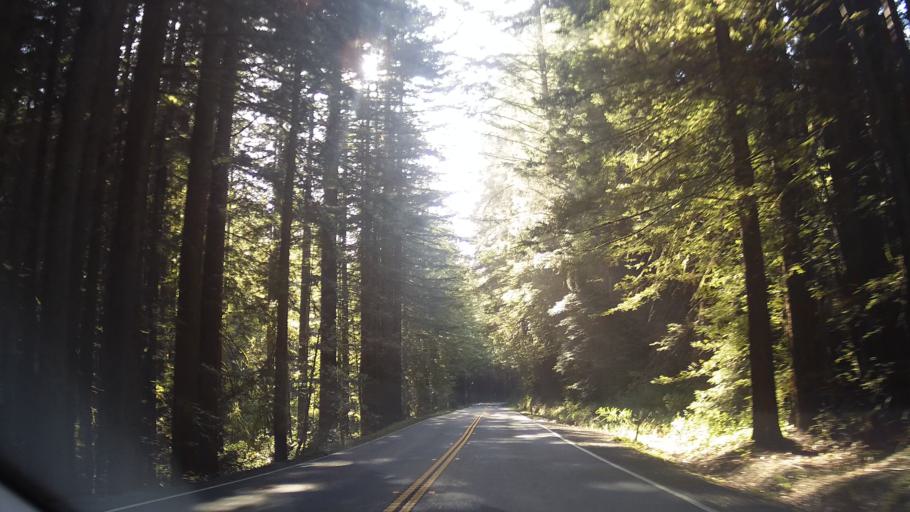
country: US
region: California
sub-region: Mendocino County
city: Fort Bragg
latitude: 39.3472
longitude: -123.5987
